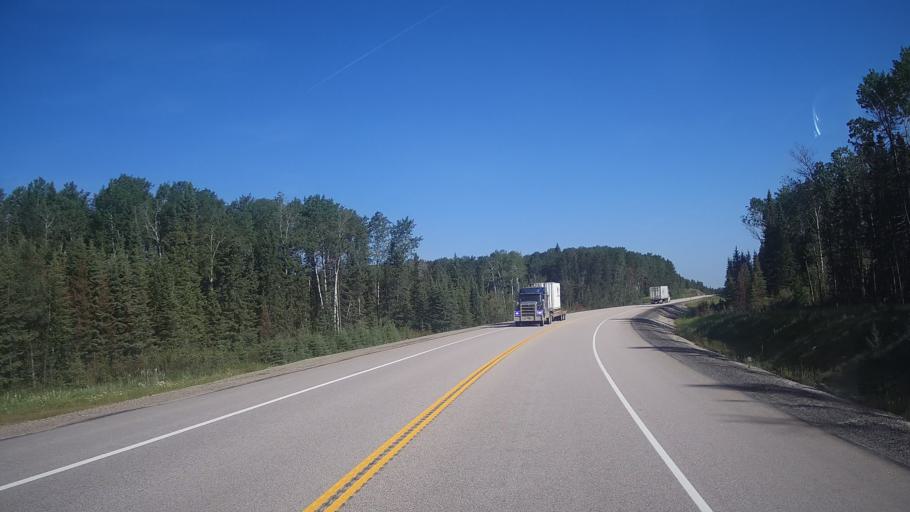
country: CA
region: Ontario
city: Dryden
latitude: 49.5749
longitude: -92.2600
